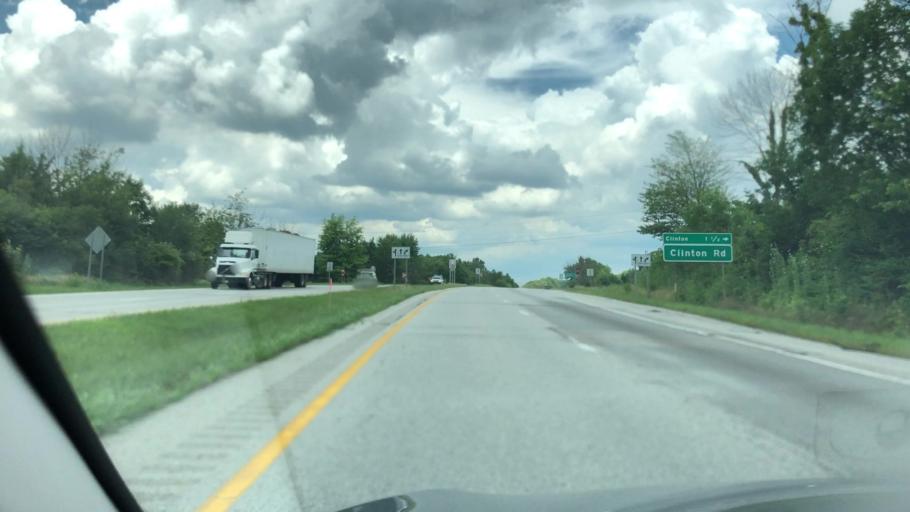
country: US
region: Ohio
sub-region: Summit County
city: Clinton
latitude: 40.9410
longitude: -81.6575
